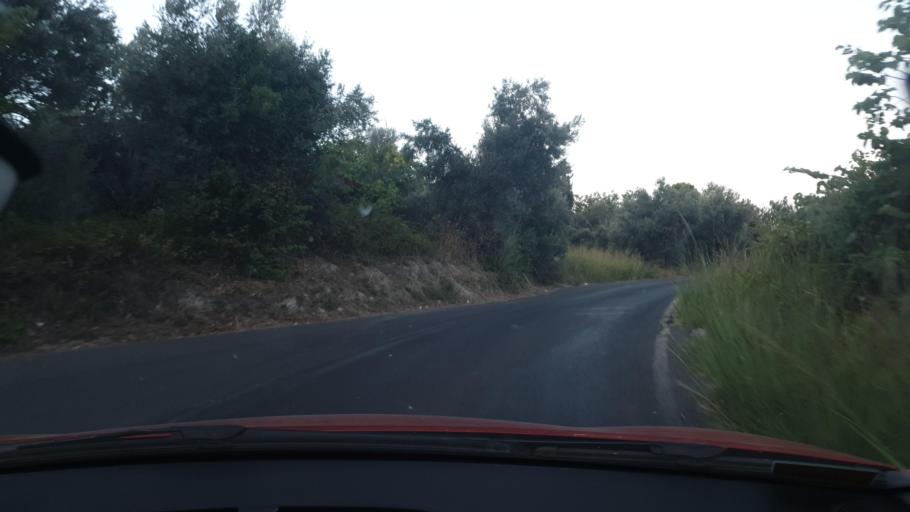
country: GR
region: Central Greece
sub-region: Nomos Evvoias
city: Kymi
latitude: 38.6304
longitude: 24.1124
